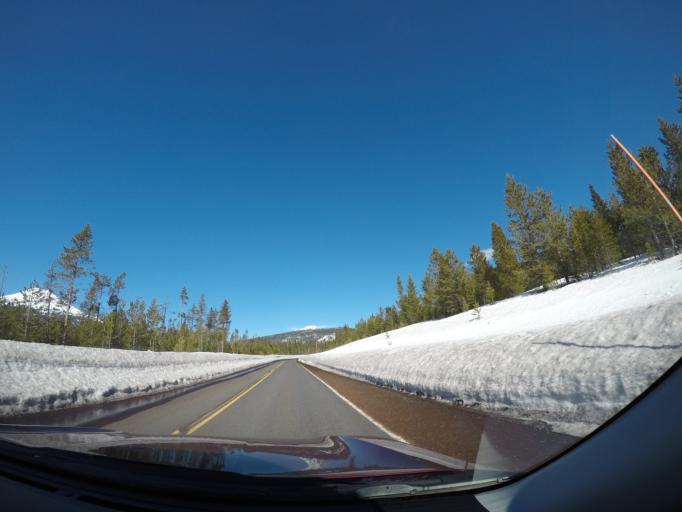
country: US
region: Oregon
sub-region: Deschutes County
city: Sunriver
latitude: 43.9636
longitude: -121.6161
